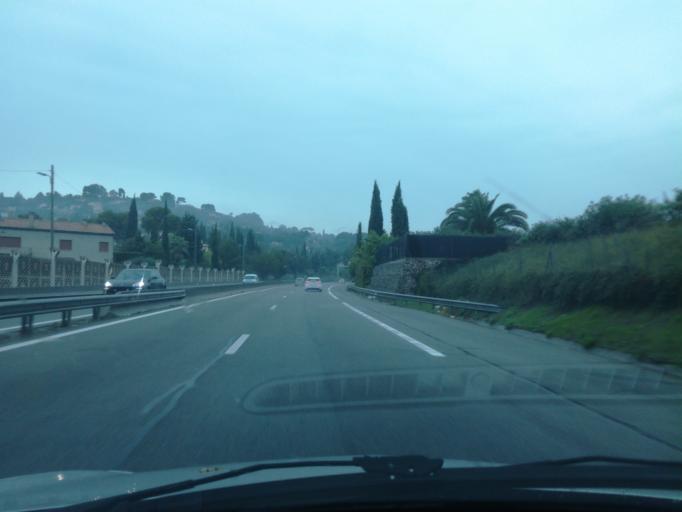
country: FR
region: Provence-Alpes-Cote d'Azur
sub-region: Departement des Alpes-Maritimes
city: Mougins
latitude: 43.5922
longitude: 7.0003
